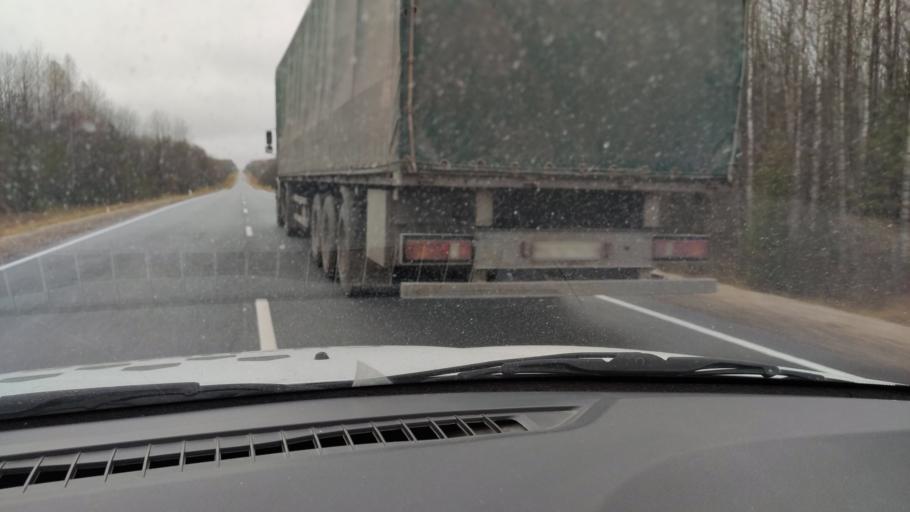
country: RU
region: Kirov
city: Chernaya Kholunitsa
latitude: 58.8027
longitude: 51.8568
